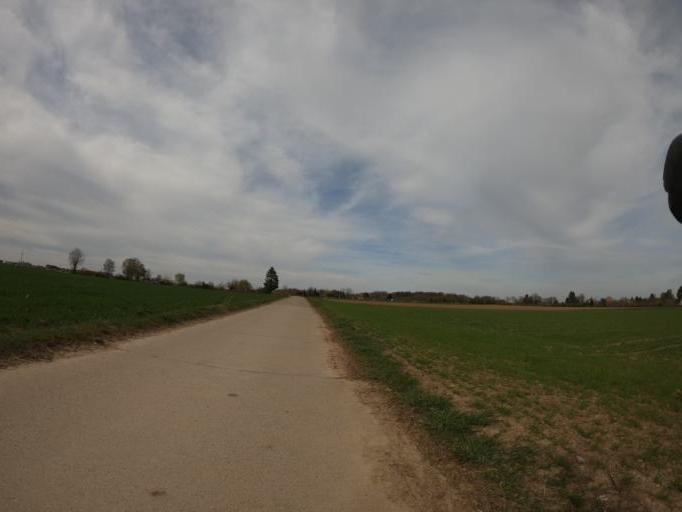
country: DE
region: Baden-Wuerttemberg
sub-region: Regierungsbezirk Stuttgart
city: Ostfildern
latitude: 48.7310
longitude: 9.2376
